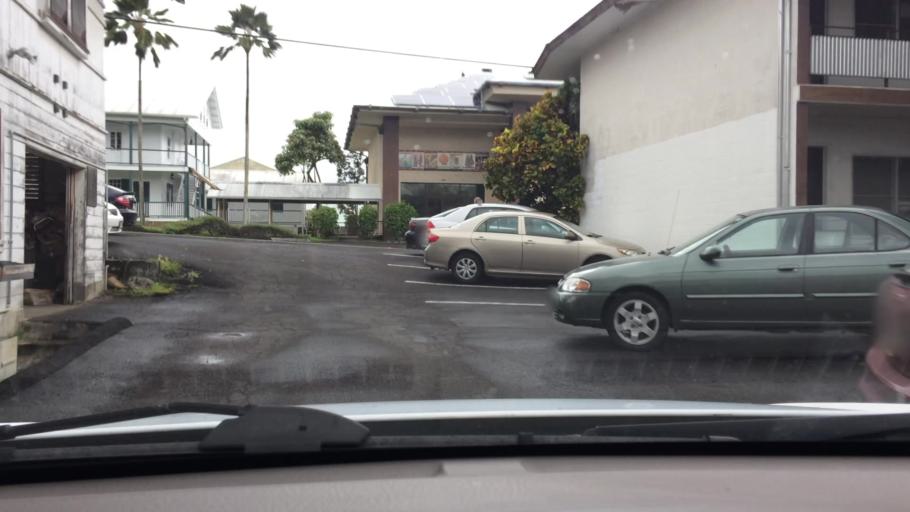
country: US
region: Hawaii
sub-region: Hawaii County
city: Hilo
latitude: 19.7217
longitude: -155.0907
